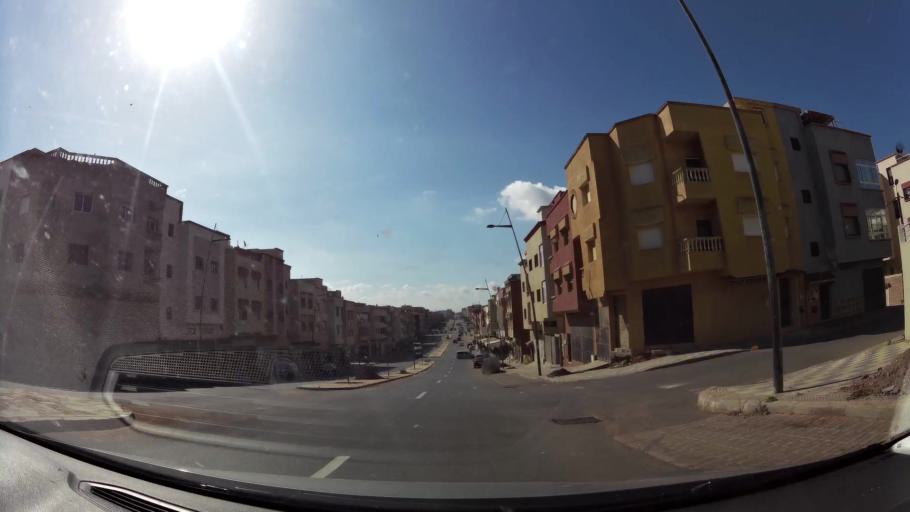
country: MA
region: Rabat-Sale-Zemmour-Zaer
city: Sale
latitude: 34.0737
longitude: -6.7983
